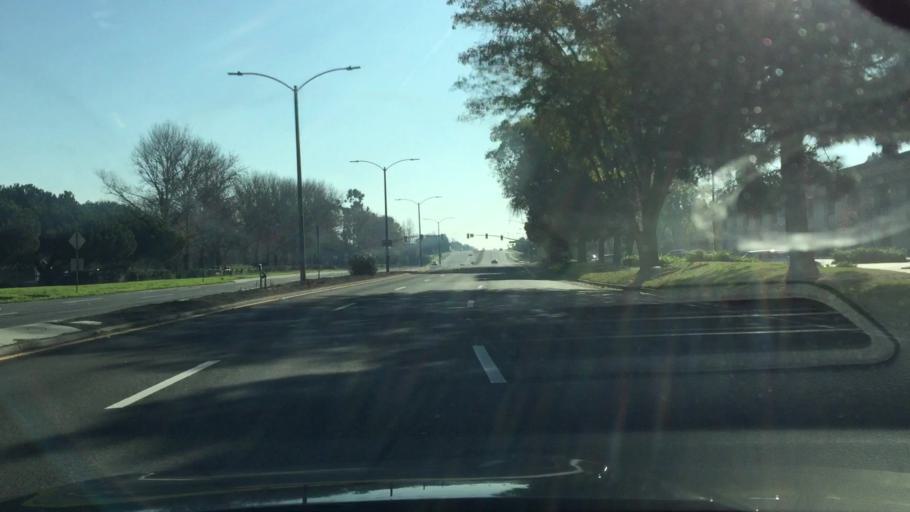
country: US
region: California
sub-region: Santa Clara County
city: Sunnyvale
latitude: 37.4136
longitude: -122.0015
